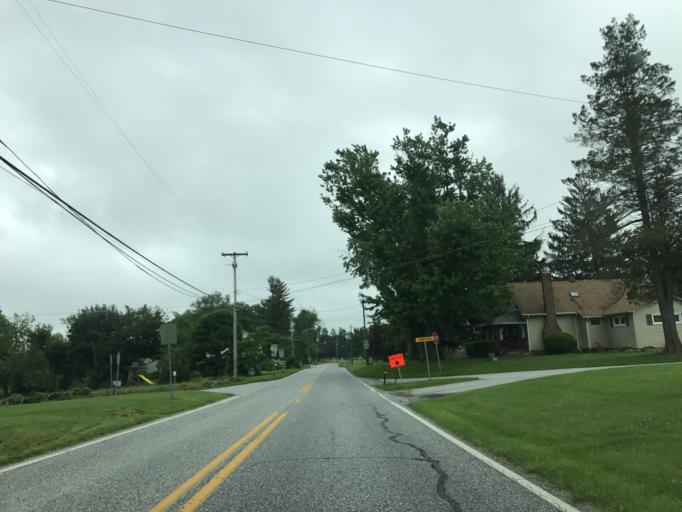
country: US
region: Pennsylvania
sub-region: York County
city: Susquehanna Trails
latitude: 39.7383
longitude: -76.4523
